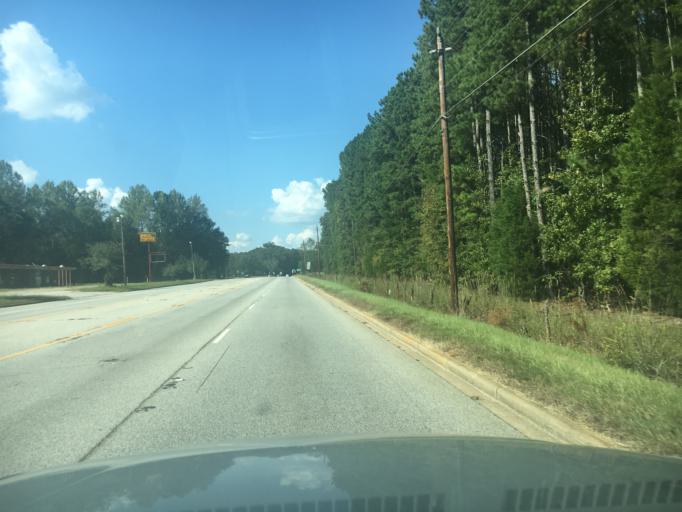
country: US
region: South Carolina
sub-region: Greenwood County
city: Ware Shoals
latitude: 34.3747
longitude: -82.2237
